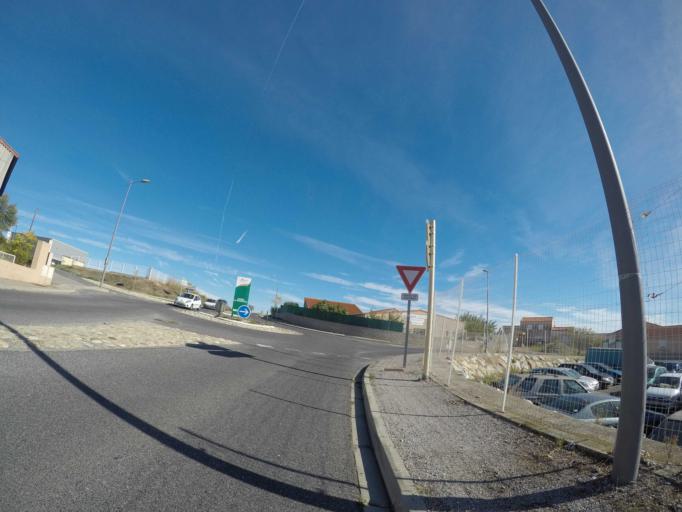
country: FR
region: Languedoc-Roussillon
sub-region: Departement des Pyrenees-Orientales
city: Trouillas
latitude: 42.6165
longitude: 2.8113
